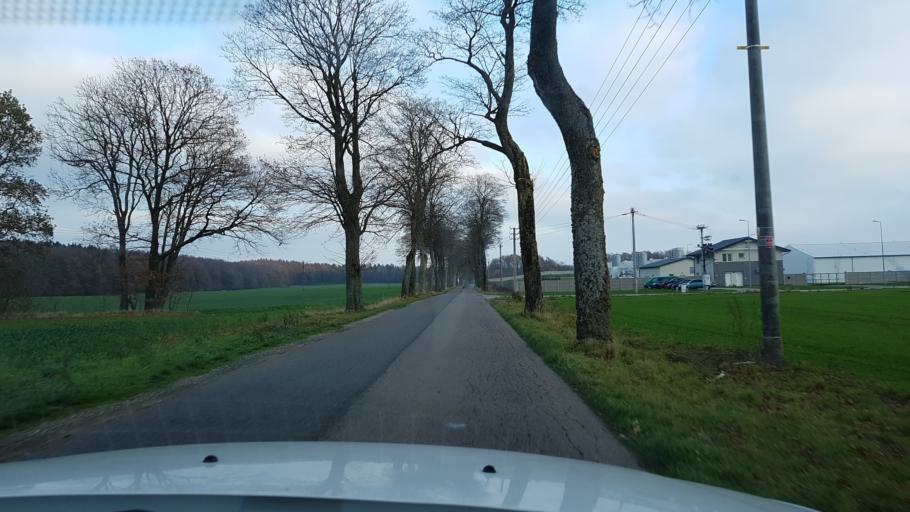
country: PL
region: West Pomeranian Voivodeship
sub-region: Powiat kolobrzeski
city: Goscino
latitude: 54.0528
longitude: 15.7026
